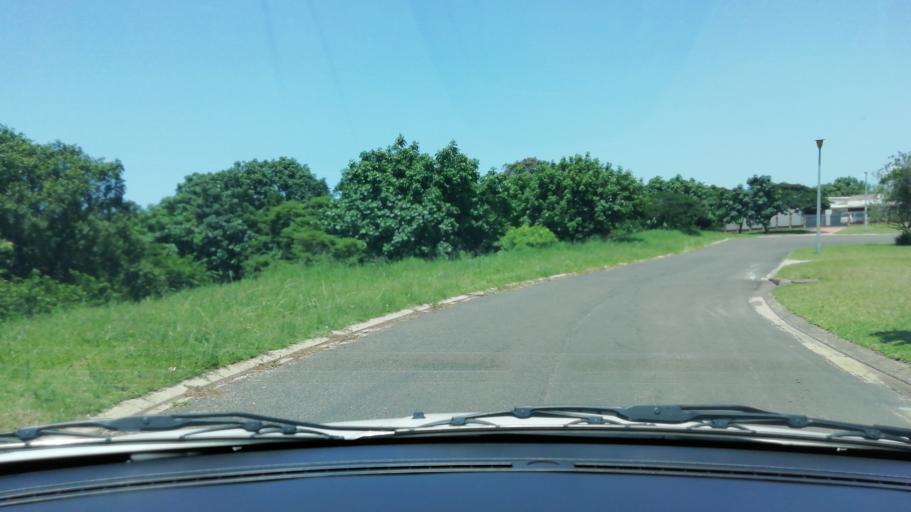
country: ZA
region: KwaZulu-Natal
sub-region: uThungulu District Municipality
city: Richards Bay
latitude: -28.7364
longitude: 32.0599
